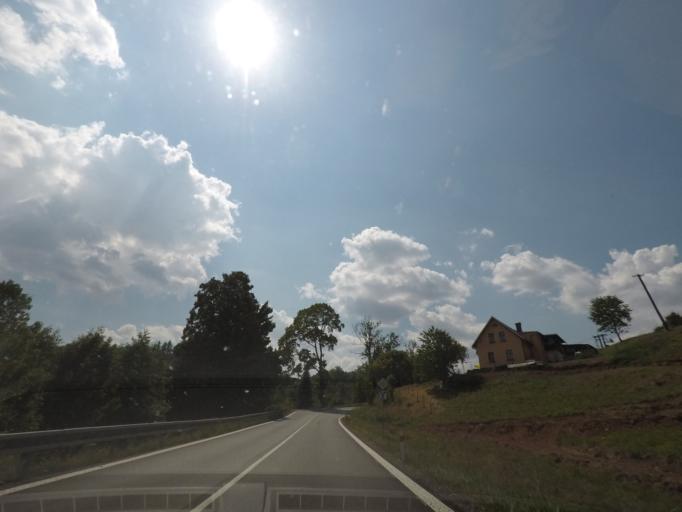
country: CZ
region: Kralovehradecky
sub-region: Okres Trutnov
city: Hostinne
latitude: 50.5173
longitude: 15.7550
